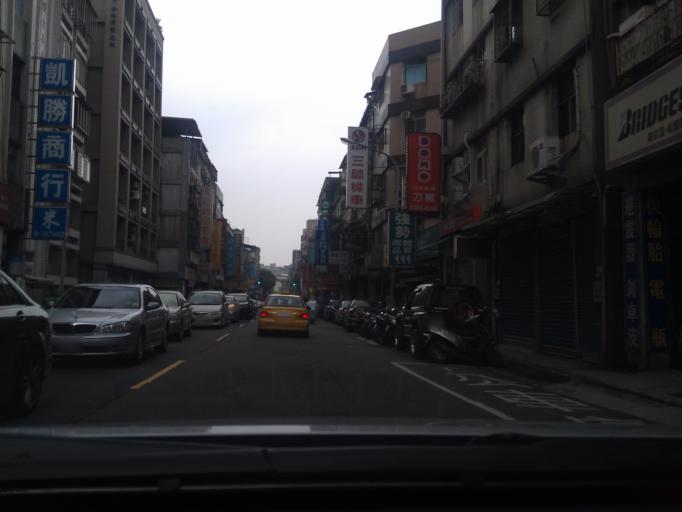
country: TW
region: Taipei
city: Taipei
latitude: 25.0213
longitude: 121.5251
